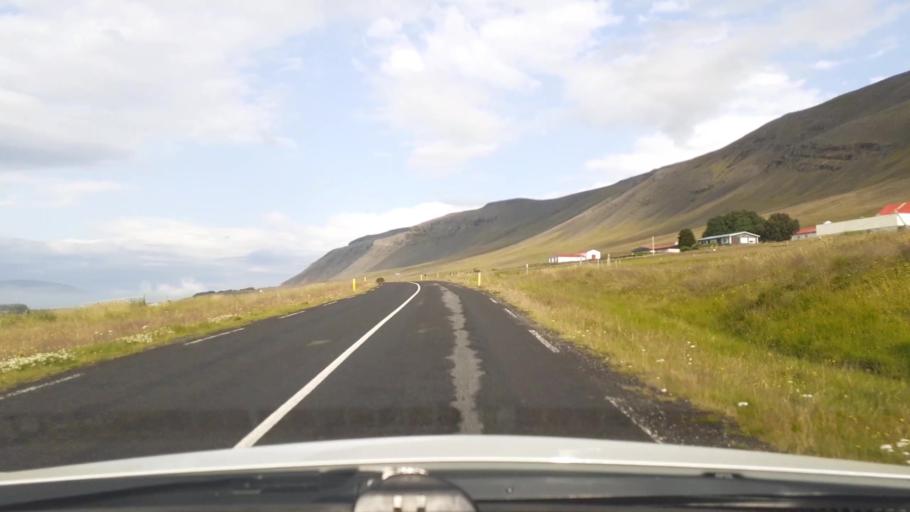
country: IS
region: Capital Region
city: Mosfellsbaer
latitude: 64.3417
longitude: -21.5561
